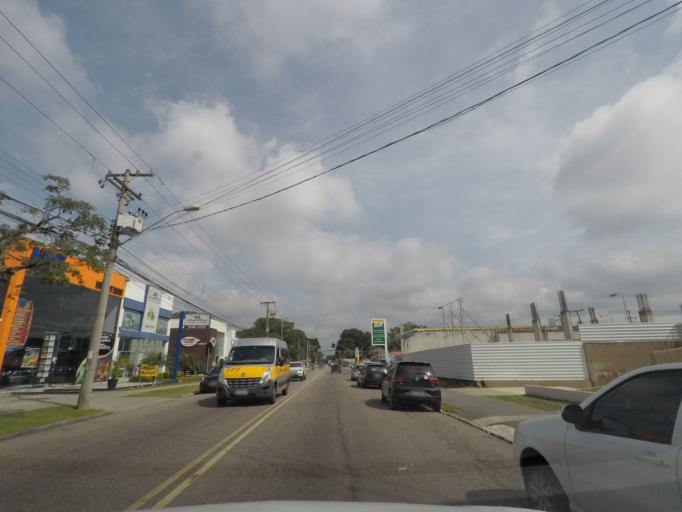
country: BR
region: Parana
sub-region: Curitiba
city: Curitiba
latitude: -25.4753
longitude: -49.3025
